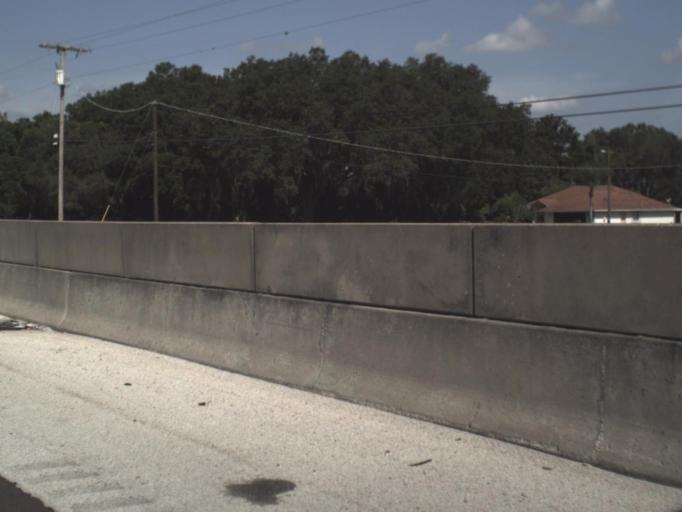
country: US
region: Florida
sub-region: Hillsborough County
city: Plant City
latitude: 28.0371
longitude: -82.0851
